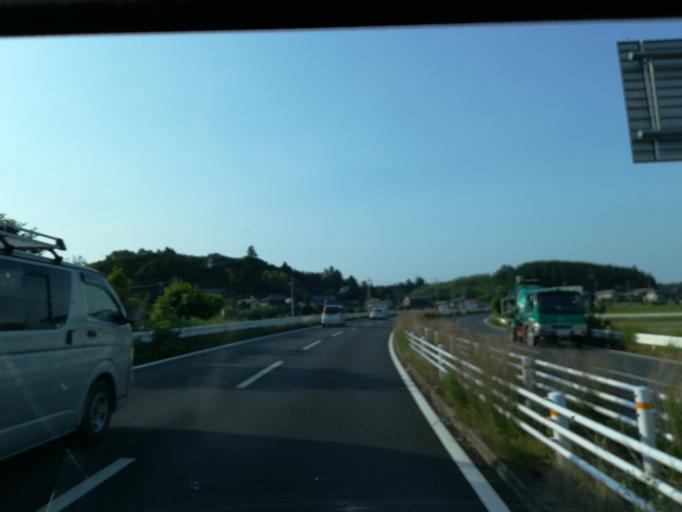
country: JP
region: Saitama
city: Kumagaya
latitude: 36.0818
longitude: 139.3575
